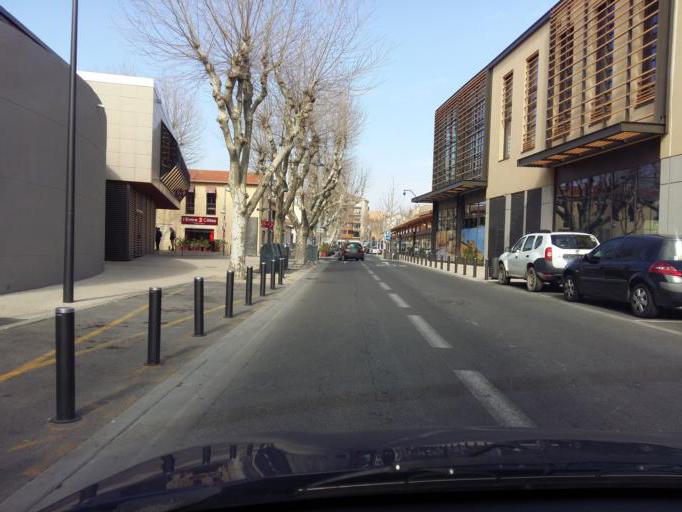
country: FR
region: Provence-Alpes-Cote d'Azur
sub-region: Departement des Bouches-du-Rhone
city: Salon-de-Provence
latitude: 43.6379
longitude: 5.0941
